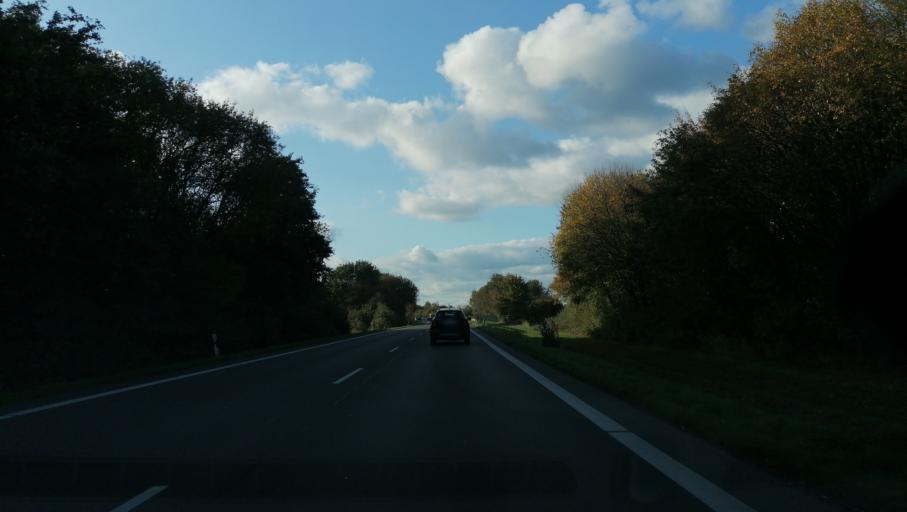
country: DE
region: North Rhine-Westphalia
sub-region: Regierungsbezirk Munster
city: Recklinghausen
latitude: 51.6330
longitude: 7.2135
